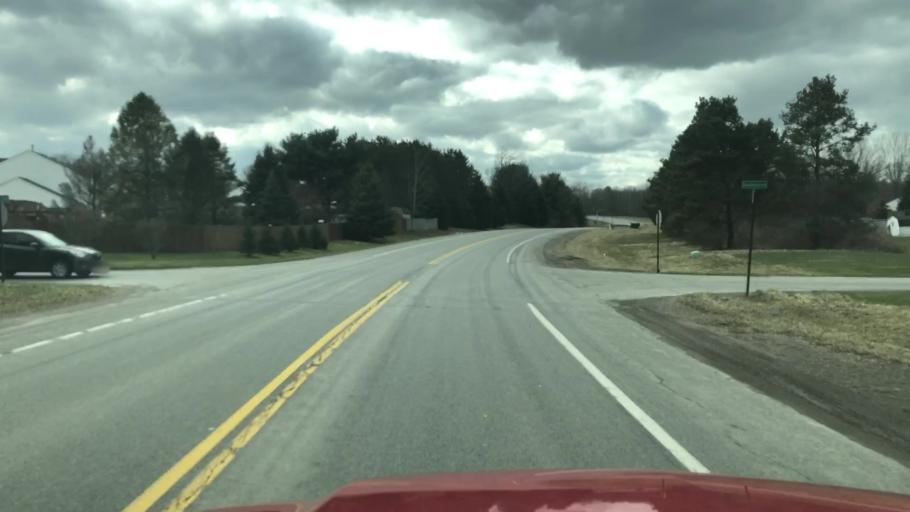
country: US
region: New York
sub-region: Wayne County
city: Macedon
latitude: 43.1264
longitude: -77.3463
